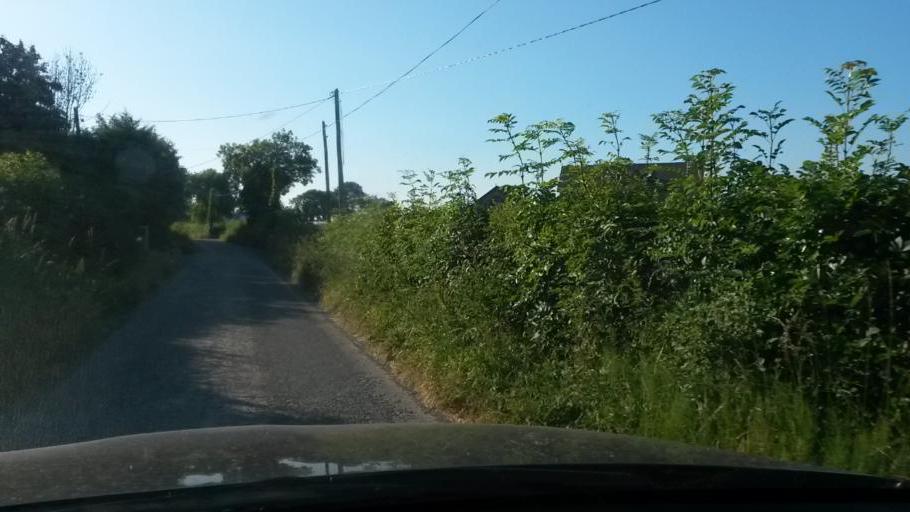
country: IE
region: Leinster
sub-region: Fingal County
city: Swords
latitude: 53.4962
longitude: -6.2846
